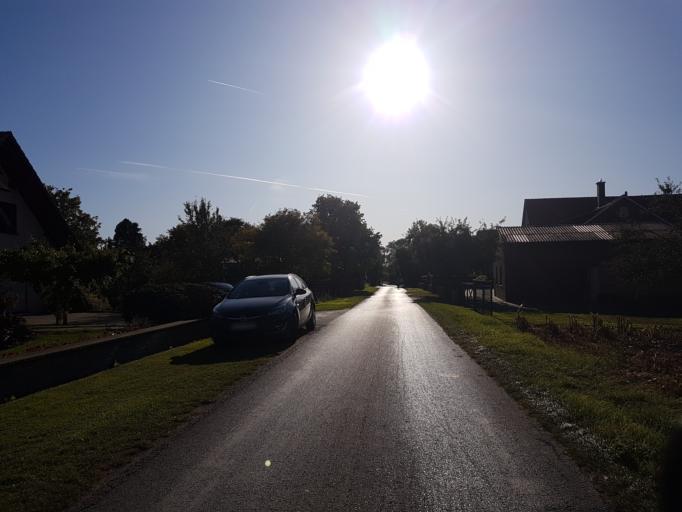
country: DE
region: North Rhine-Westphalia
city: Bad Oeynhausen
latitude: 52.2377
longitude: 8.8513
